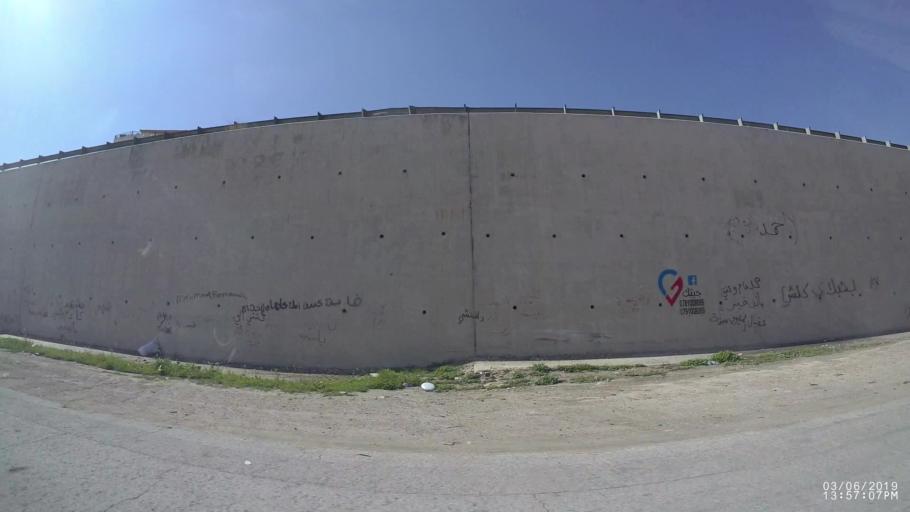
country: JO
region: Zarqa
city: Zarqa
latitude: 32.0355
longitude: 36.1020
